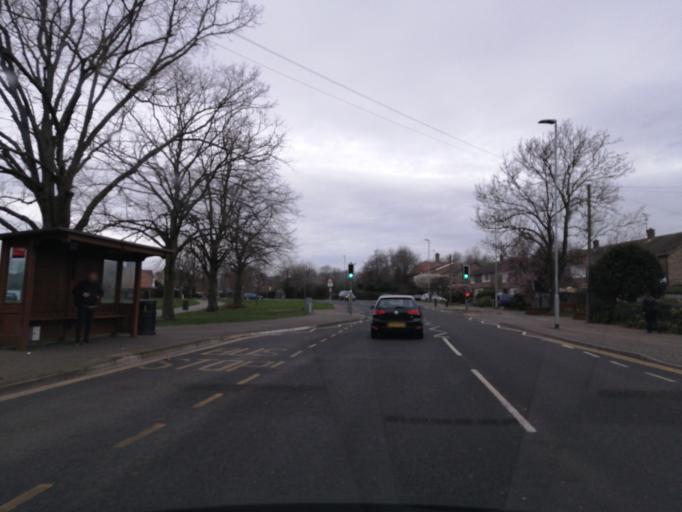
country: GB
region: England
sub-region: Peterborough
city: Eye
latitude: 52.5892
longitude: -0.2169
